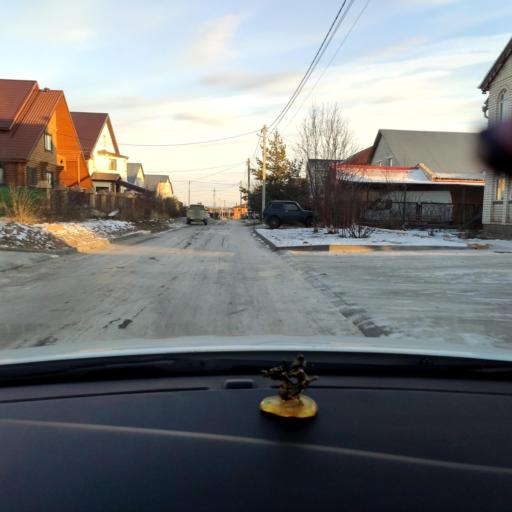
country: RU
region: Tatarstan
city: Stolbishchi
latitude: 55.6059
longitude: 49.1450
